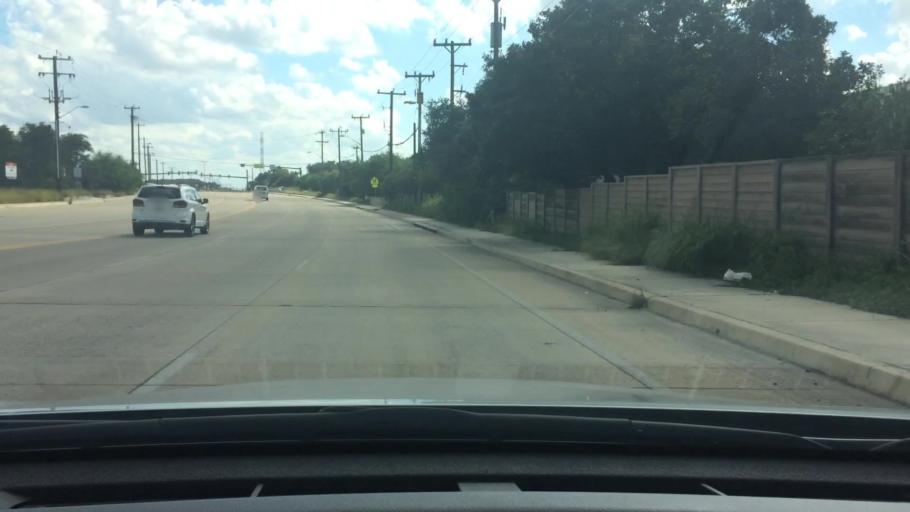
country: US
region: Texas
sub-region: Bexar County
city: Hollywood Park
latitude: 29.6412
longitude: -98.4250
